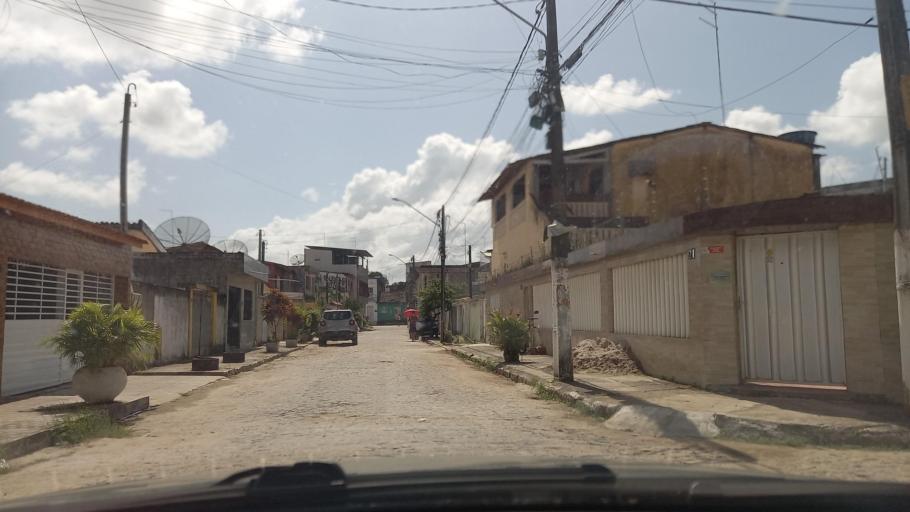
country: BR
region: Pernambuco
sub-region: Goiana
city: Goiana
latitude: -7.5622
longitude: -34.9957
